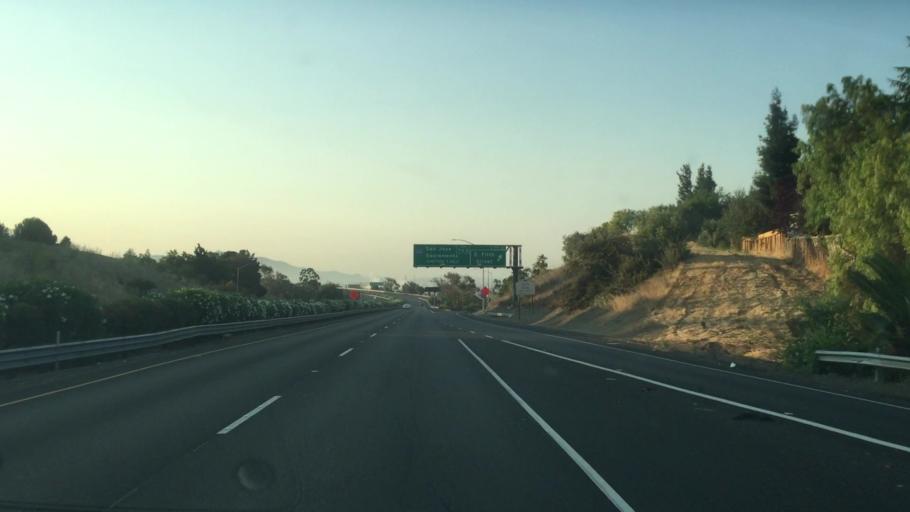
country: US
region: California
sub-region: Solano County
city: Benicia
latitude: 38.0564
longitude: -122.1485
